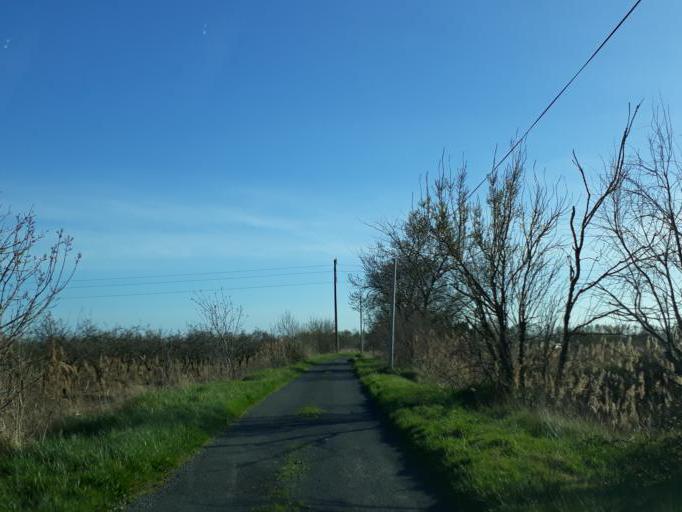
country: FR
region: Languedoc-Roussillon
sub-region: Departement de l'Herault
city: Agde
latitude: 43.3234
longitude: 3.4528
